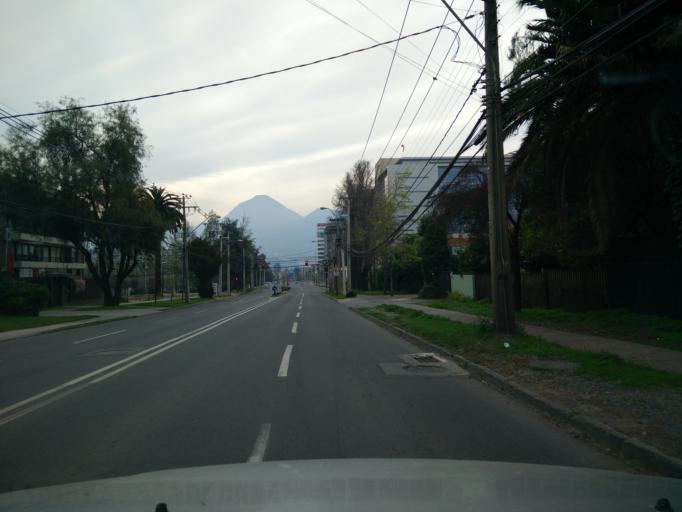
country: CL
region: Santiago Metropolitan
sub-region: Provincia de Santiago
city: Villa Presidente Frei, Nunoa, Santiago, Chile
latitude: -33.3867
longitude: -70.5303
